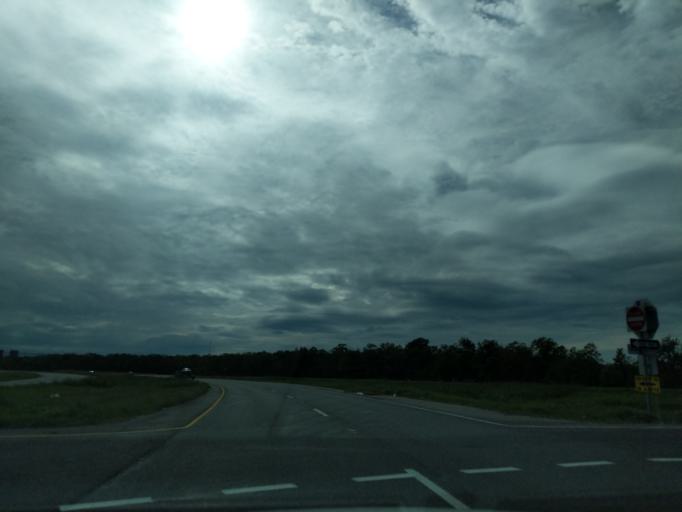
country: US
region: Louisiana
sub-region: Saint Bernard Parish
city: Chalmette
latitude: 30.0176
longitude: -89.9421
